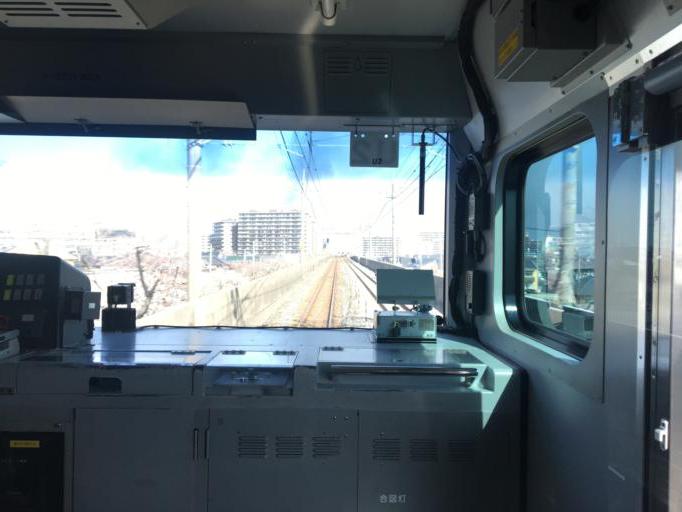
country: JP
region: Ibaraki
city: Koga
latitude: 36.1868
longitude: 139.7119
